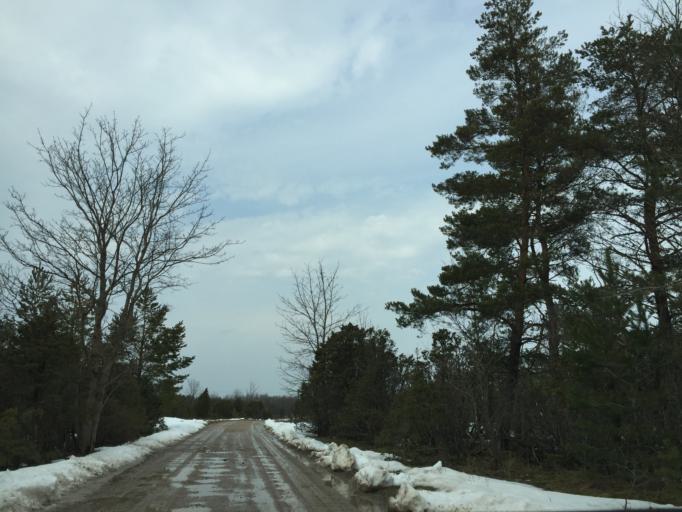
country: EE
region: Saare
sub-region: Kuressaare linn
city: Kuressaare
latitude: 58.4334
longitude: 22.1427
